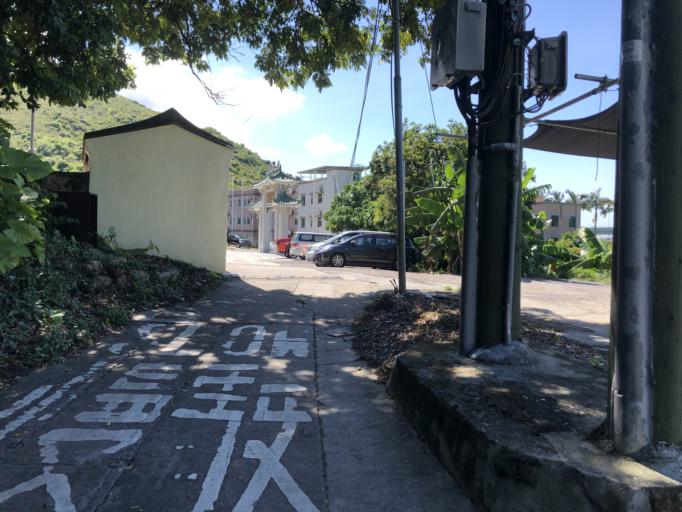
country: HK
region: Tuen Mun
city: Tuen Mun
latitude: 22.2957
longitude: 113.9718
